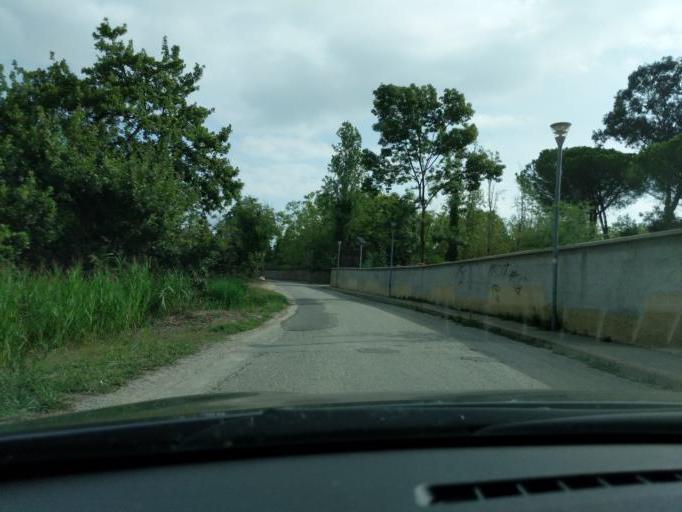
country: FR
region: Corsica
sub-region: Departement de la Haute-Corse
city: Ghisonaccia
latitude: 41.9992
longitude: 9.4427
